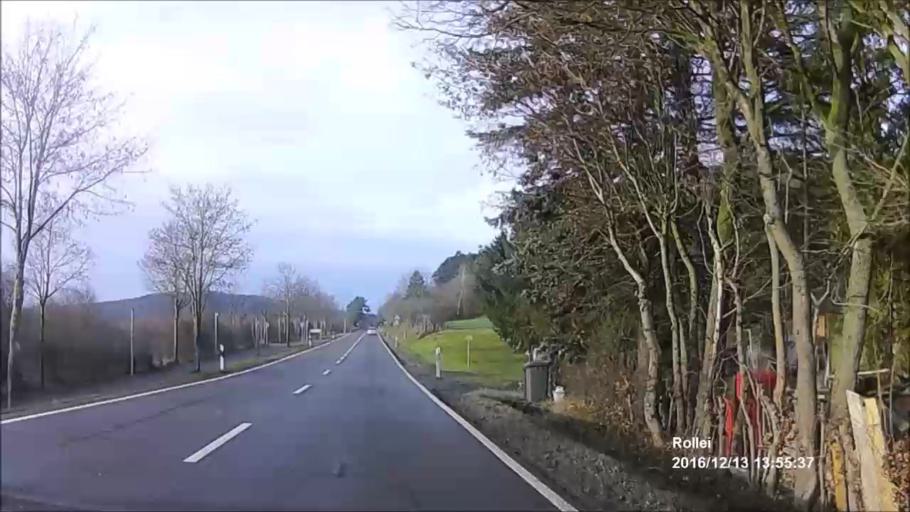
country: DE
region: Thuringia
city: Bad Berka
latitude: 50.9067
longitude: 11.2745
